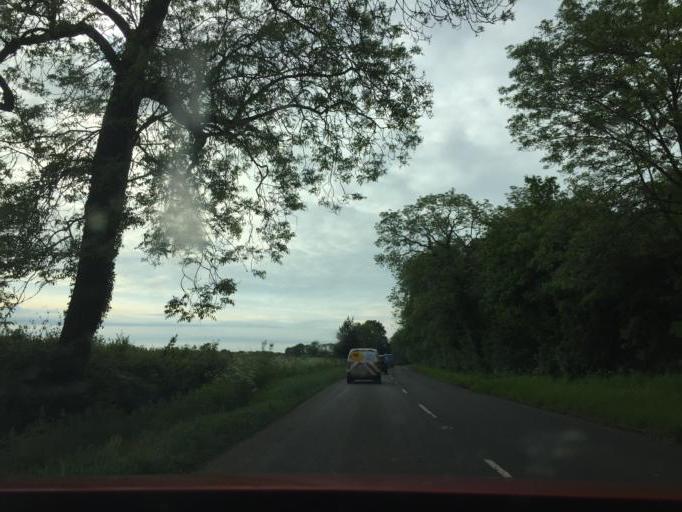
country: GB
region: England
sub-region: Leicestershire
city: Sapcote
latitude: 52.4588
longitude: -1.2857
